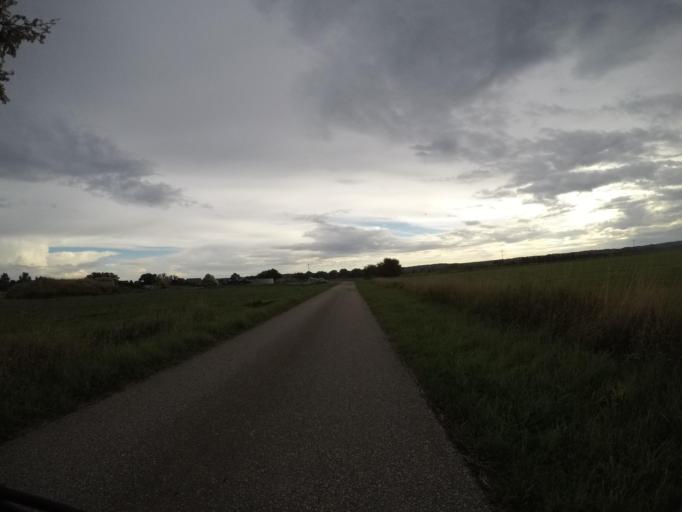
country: DE
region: Lower Saxony
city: Neu Darchau
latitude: 53.2542
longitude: 10.8743
